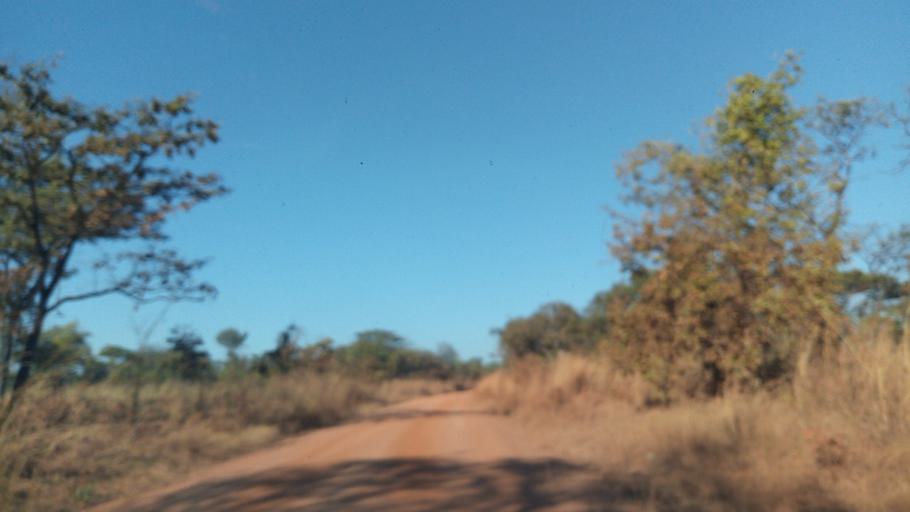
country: ZM
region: Luapula
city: Mwense
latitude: -10.5628
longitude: 28.4401
